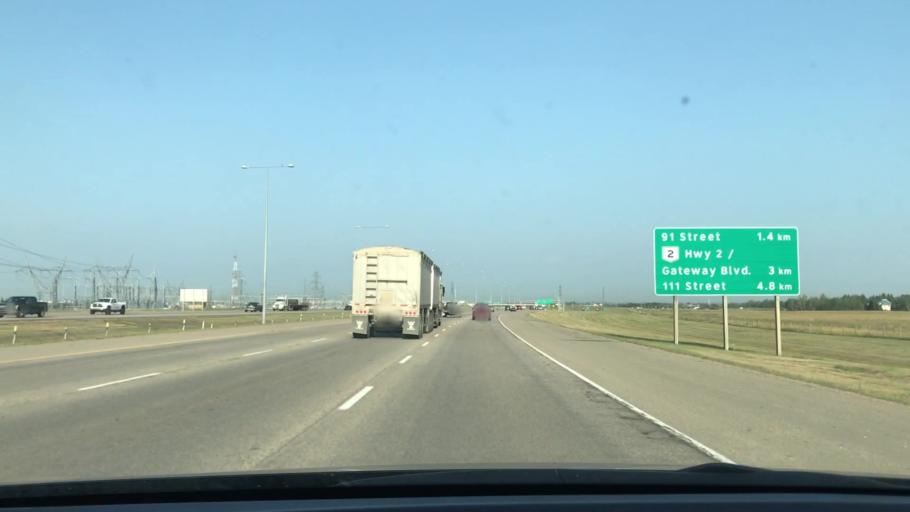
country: CA
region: Alberta
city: Beaumont
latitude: 53.4359
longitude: -113.4448
